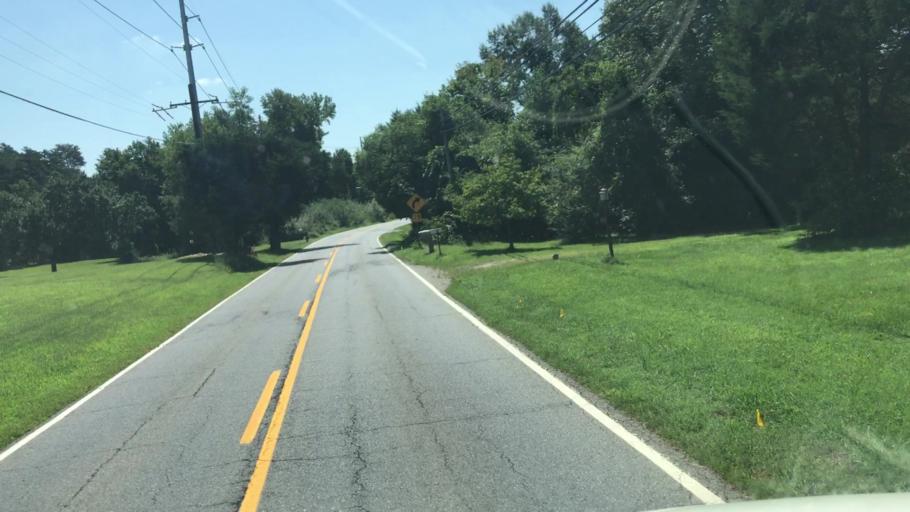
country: US
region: Maryland
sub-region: Prince George's County
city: Brandywine
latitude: 38.7151
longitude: -76.8871
